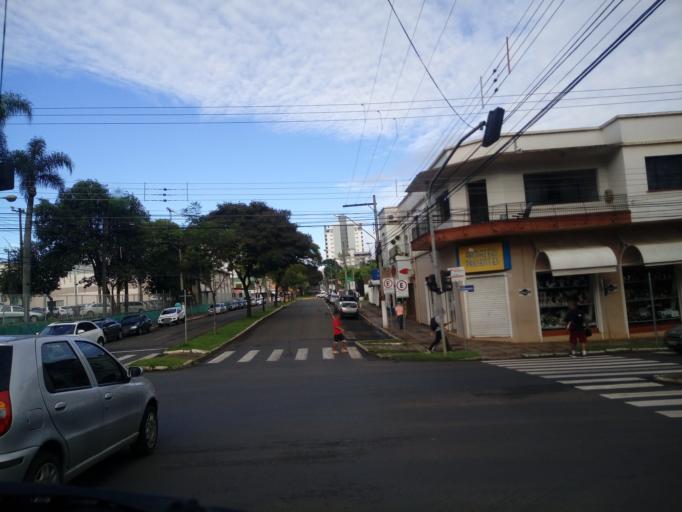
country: BR
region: Santa Catarina
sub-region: Chapeco
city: Chapeco
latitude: -27.1051
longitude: -52.6161
